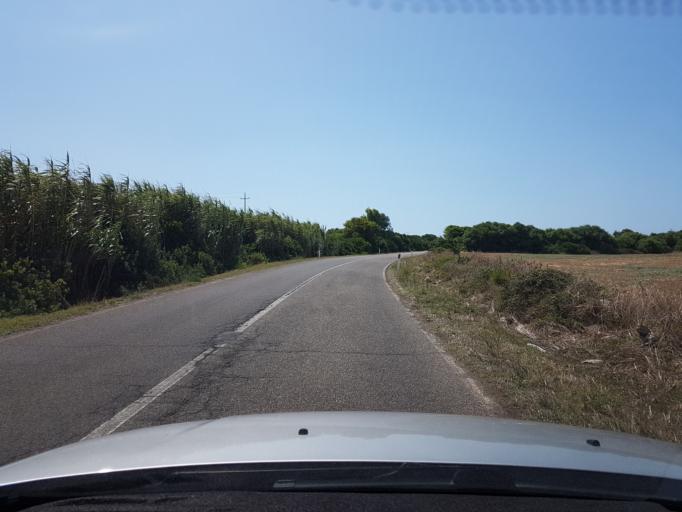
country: IT
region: Sardinia
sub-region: Provincia di Oristano
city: Riola Sardo
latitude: 40.0219
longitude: 8.4610
